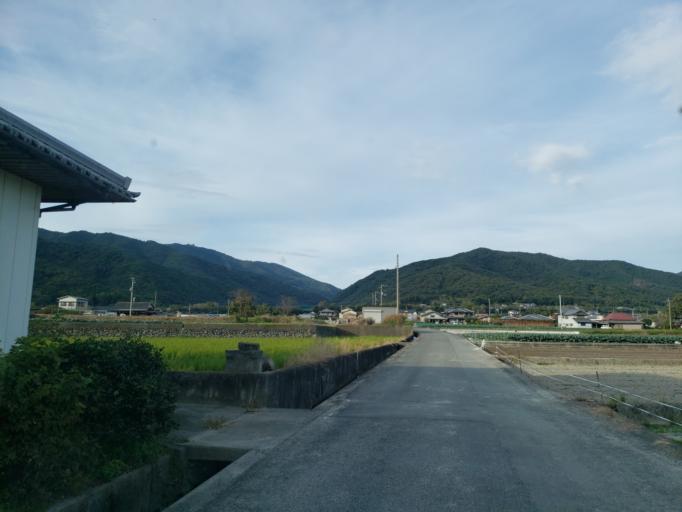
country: JP
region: Tokushima
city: Wakimachi
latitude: 34.0933
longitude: 134.2253
